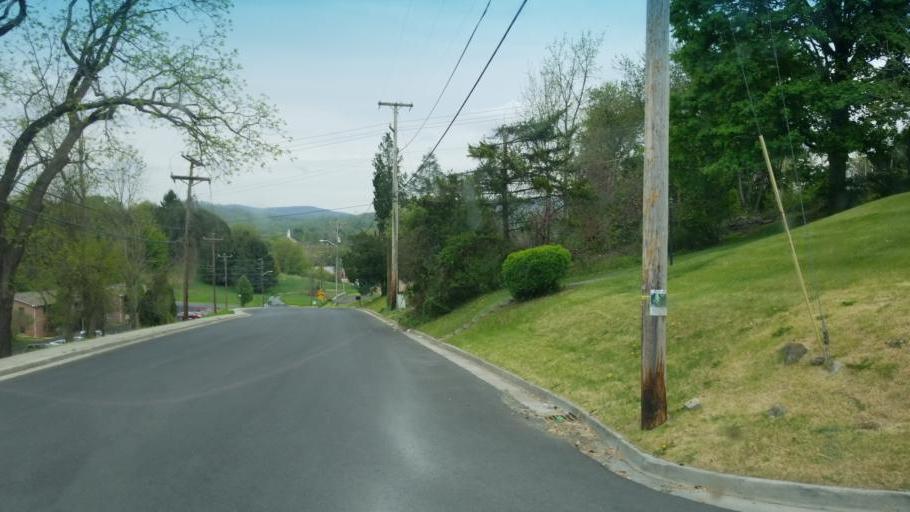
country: US
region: Virginia
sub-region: Smyth County
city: Marion
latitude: 36.8406
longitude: -81.5193
